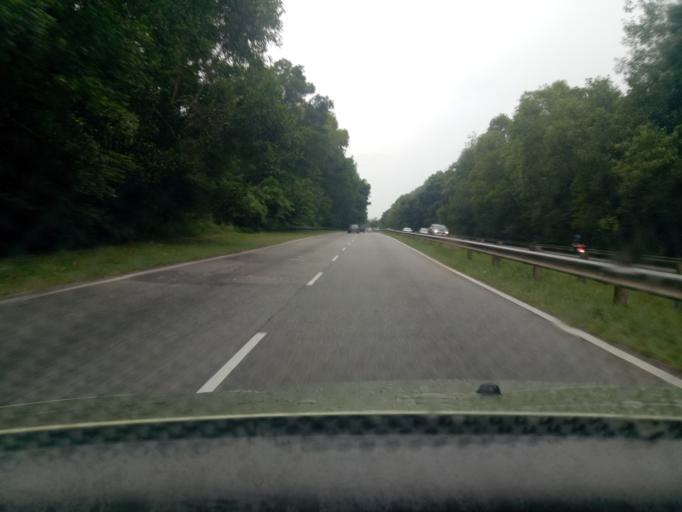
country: MY
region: Kedah
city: Sungai Petani
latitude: 5.6677
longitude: 100.5231
